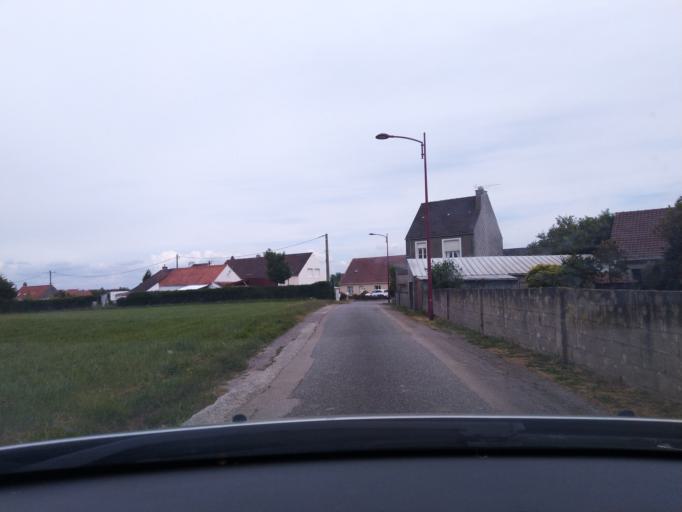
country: FR
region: Nord-Pas-de-Calais
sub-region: Departement du Pas-de-Calais
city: Ferques
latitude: 50.8376
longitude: 1.7653
